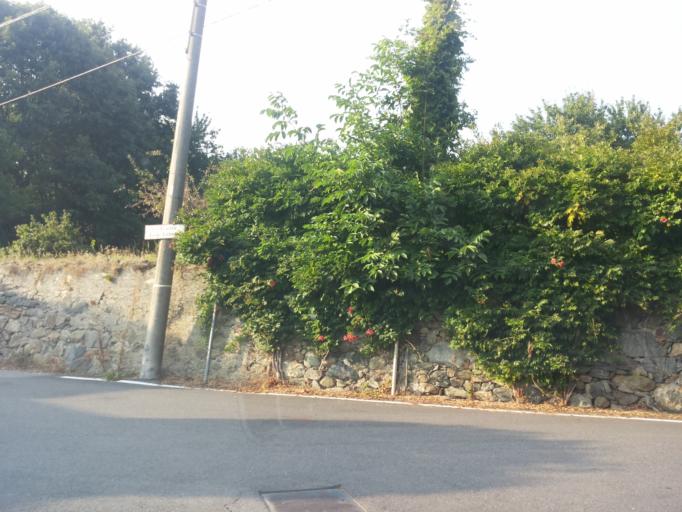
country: IT
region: Piedmont
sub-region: Provincia di Biella
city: Viverone
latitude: 45.4269
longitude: 8.0529
